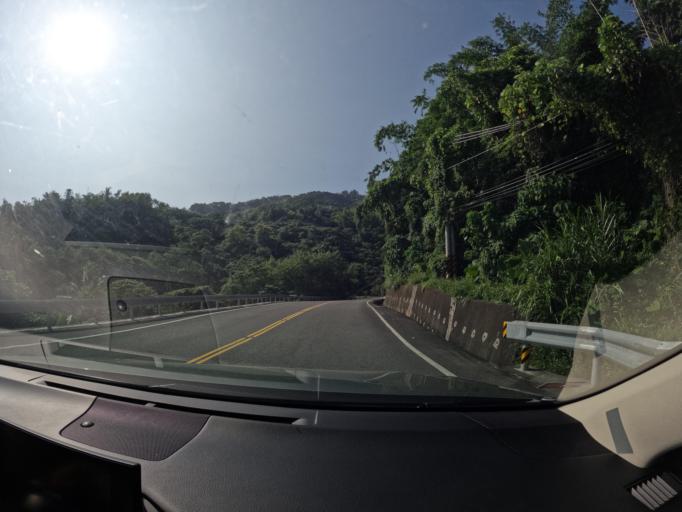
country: TW
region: Taiwan
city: Yujing
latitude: 23.0730
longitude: 120.5460
